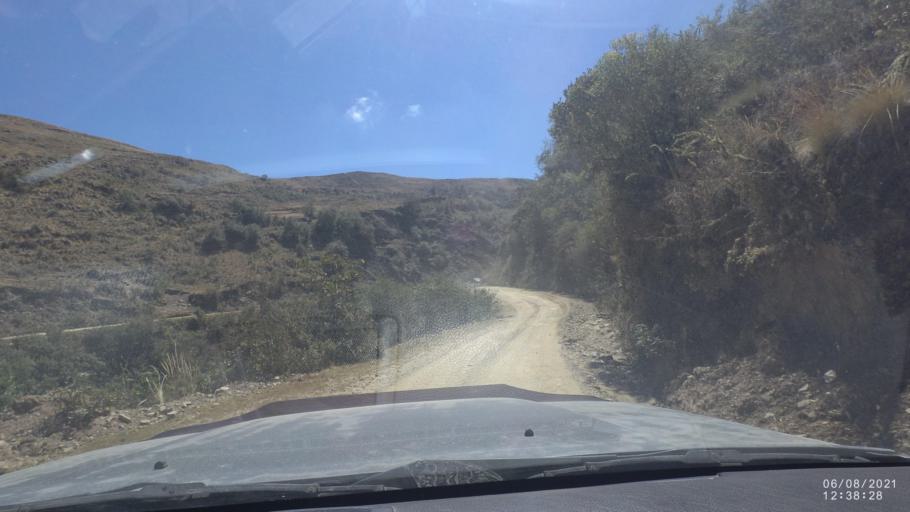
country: BO
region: Cochabamba
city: Colchani
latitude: -16.7772
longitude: -66.6617
